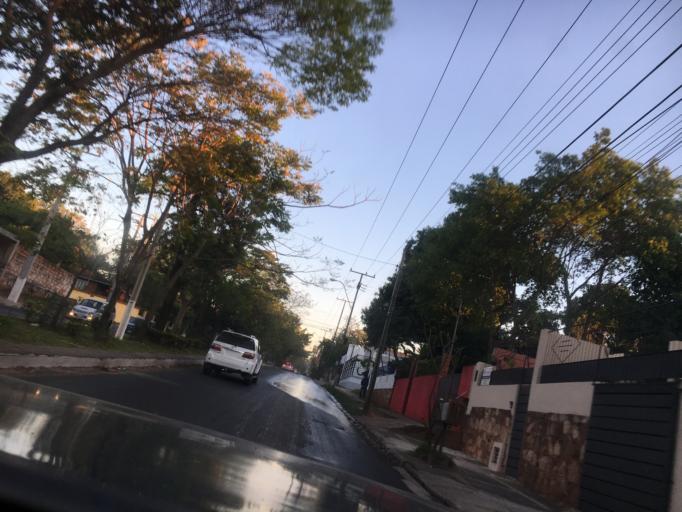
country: PY
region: Central
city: Lambare
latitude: -25.3387
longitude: -57.6057
